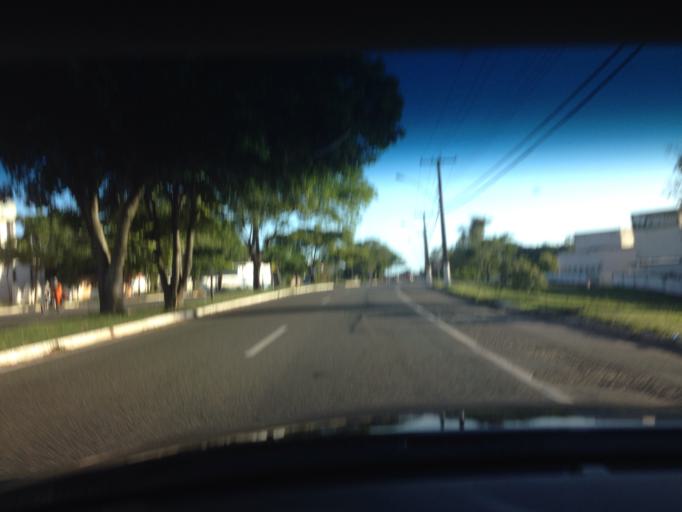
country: BR
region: Espirito Santo
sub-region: Guarapari
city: Guarapari
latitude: -20.6358
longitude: -40.5175
